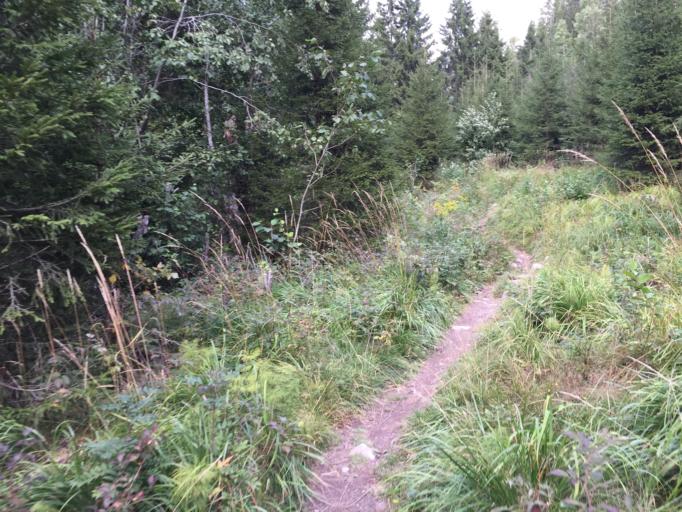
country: NO
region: Akershus
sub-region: Raelingen
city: Fjerdingby
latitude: 59.9107
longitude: 11.0377
